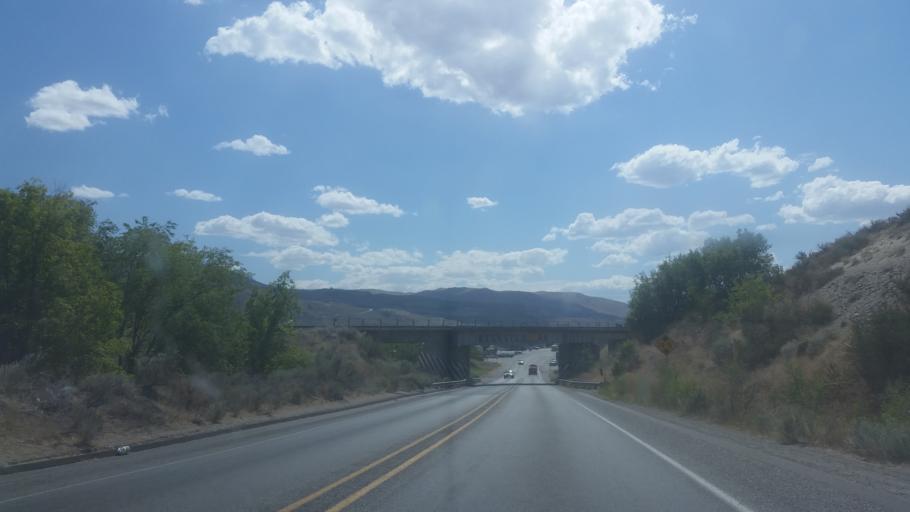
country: US
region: Washington
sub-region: Okanogan County
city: Brewster
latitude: 48.1072
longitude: -119.7780
